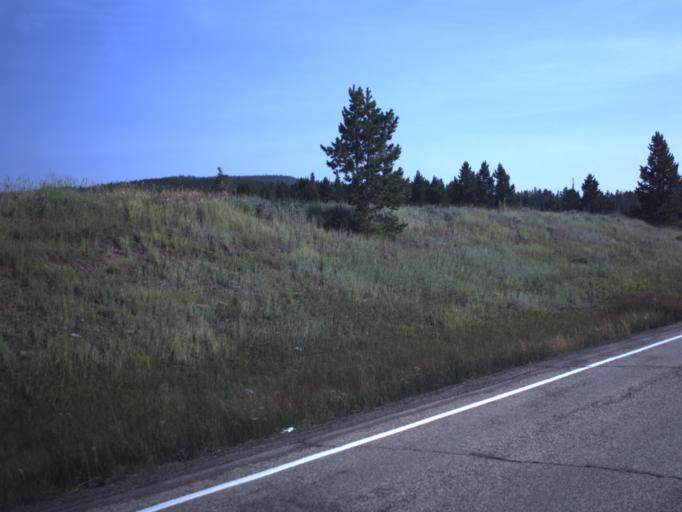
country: US
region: Utah
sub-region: Daggett County
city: Manila
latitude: 40.7903
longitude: -109.4698
